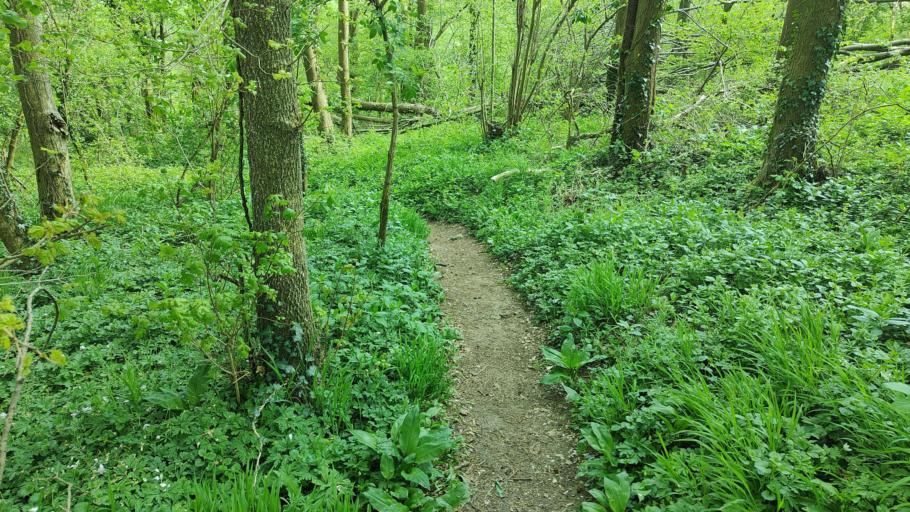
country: BE
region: Wallonia
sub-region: Province de Liege
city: La Calamine
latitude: 50.7098
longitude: 5.9899
